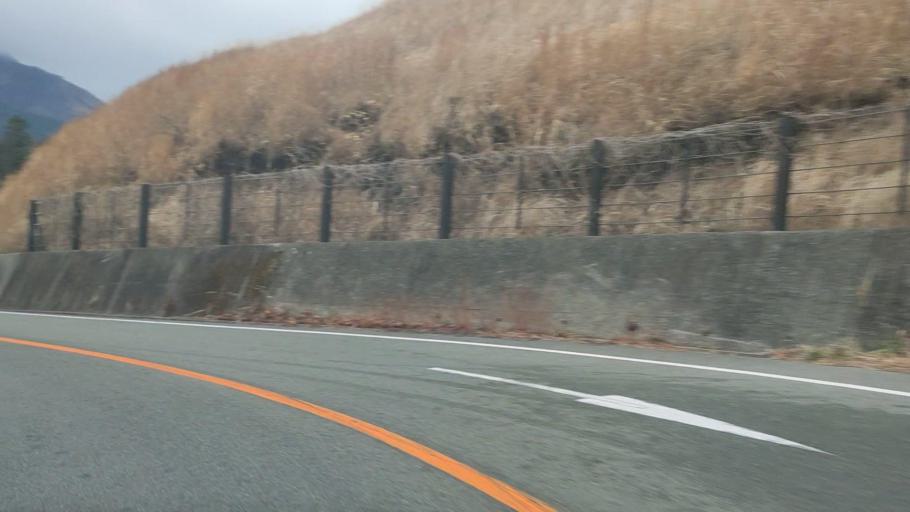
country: JP
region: Kumamoto
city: Aso
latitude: 32.9107
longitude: 131.1429
